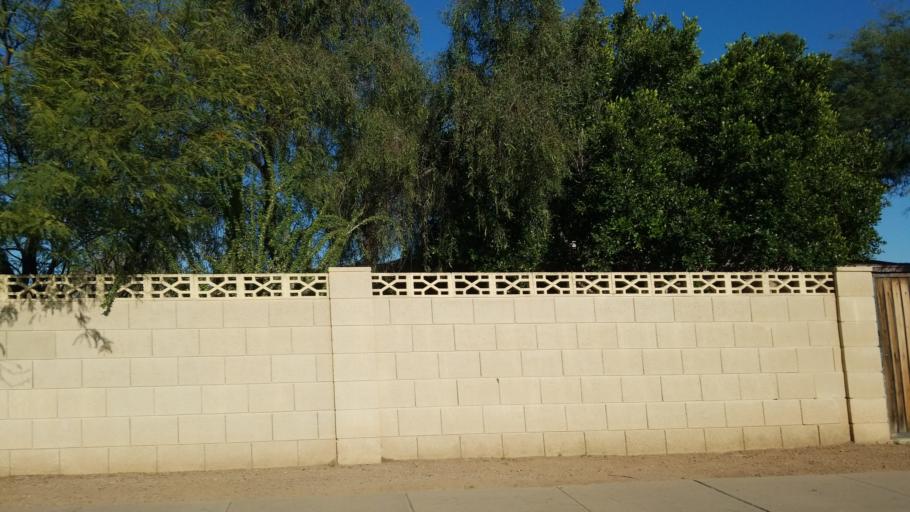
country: US
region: Arizona
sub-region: Maricopa County
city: Glendale
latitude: 33.5220
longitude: -112.1601
